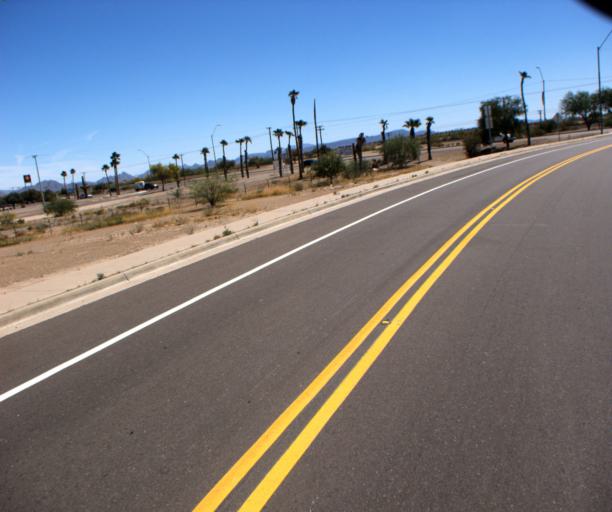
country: US
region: Arizona
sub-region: Maricopa County
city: Gila Bend
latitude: 32.9448
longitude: -112.7321
